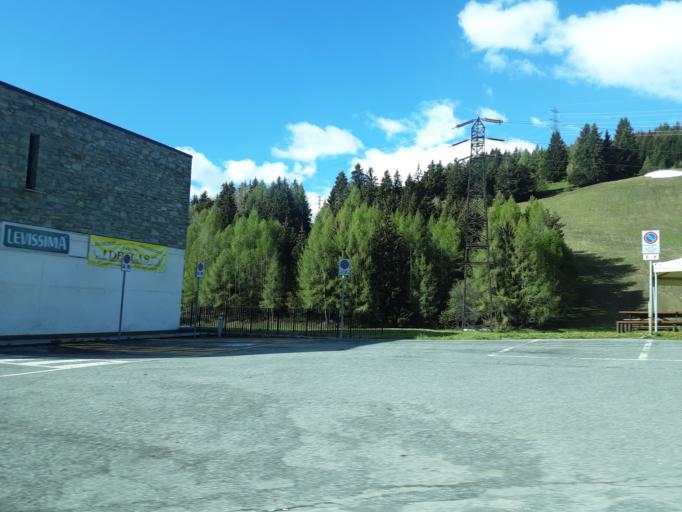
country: IT
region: Lombardy
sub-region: Provincia di Sondrio
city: Bormio
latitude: 46.4761
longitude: 10.3517
